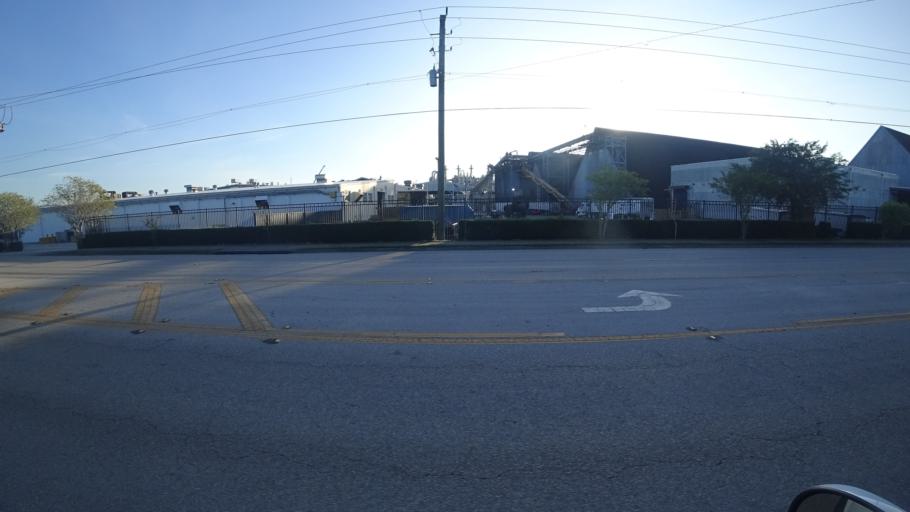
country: US
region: Florida
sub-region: Manatee County
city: West Samoset
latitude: 27.4870
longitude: -82.5549
